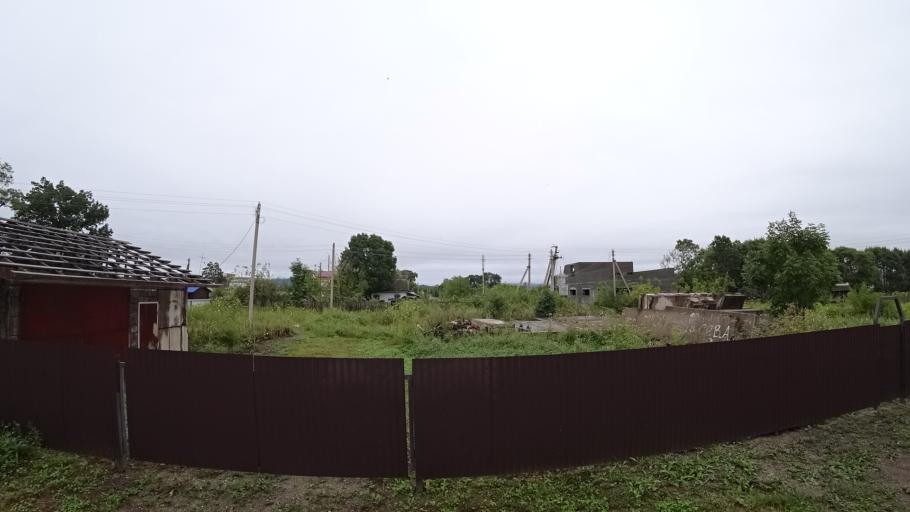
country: RU
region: Primorskiy
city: Monastyrishche
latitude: 44.2014
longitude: 132.4485
